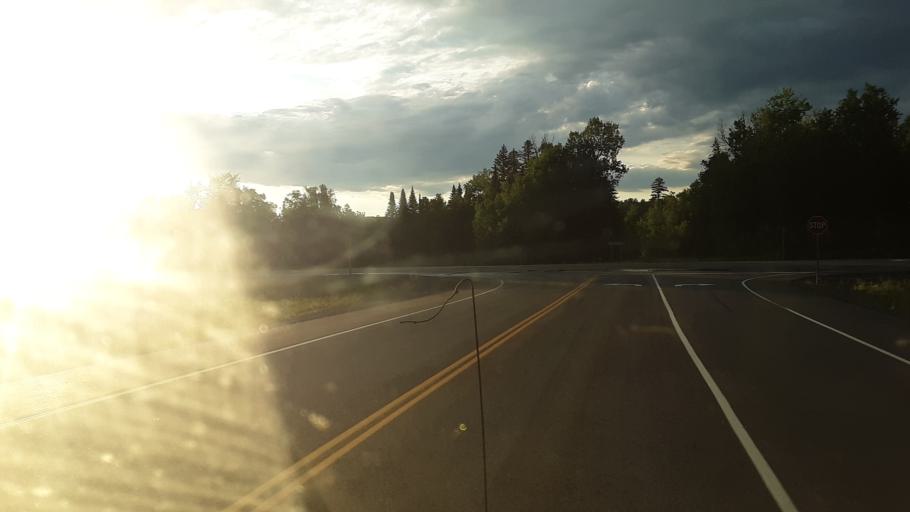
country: US
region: Maine
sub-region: Aroostook County
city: Presque Isle
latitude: 46.6943
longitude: -67.9821
